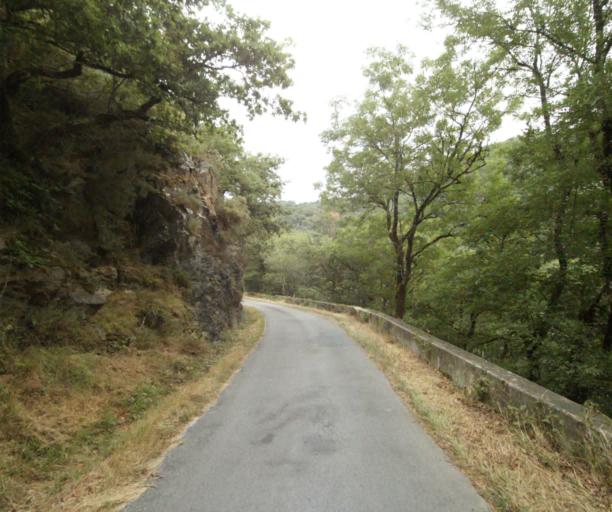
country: FR
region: Midi-Pyrenees
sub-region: Departement du Tarn
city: Soreze
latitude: 43.4178
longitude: 2.0871
